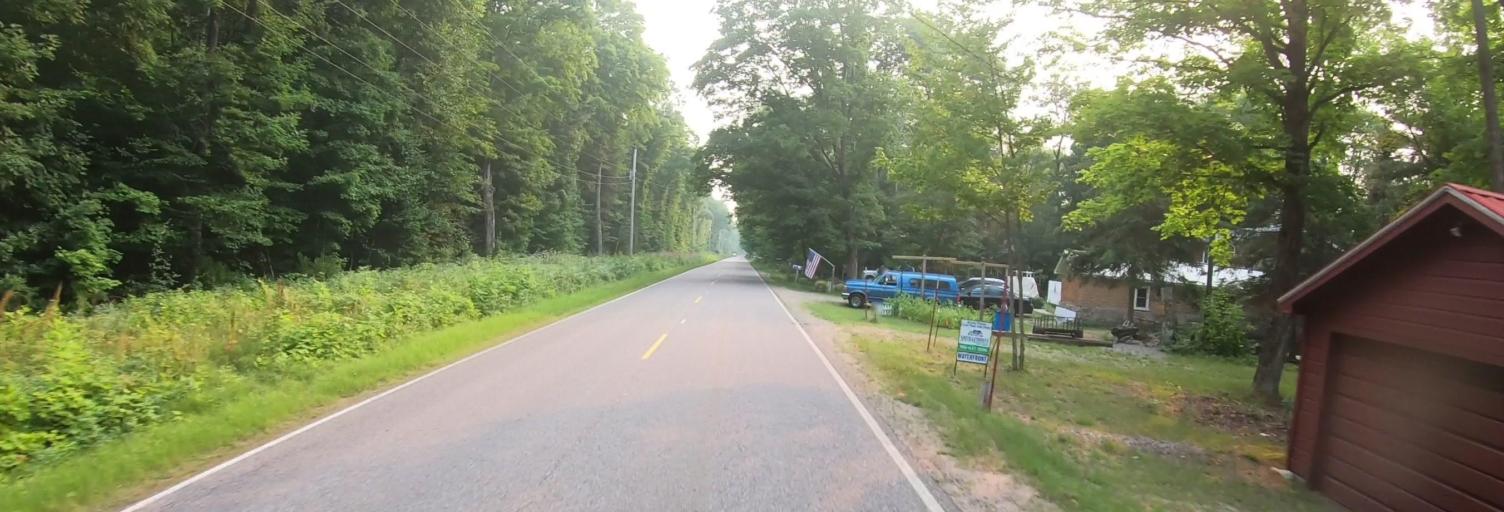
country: US
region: Michigan
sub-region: Chippewa County
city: Sault Ste. Marie
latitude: 46.4702
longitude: -84.7164
